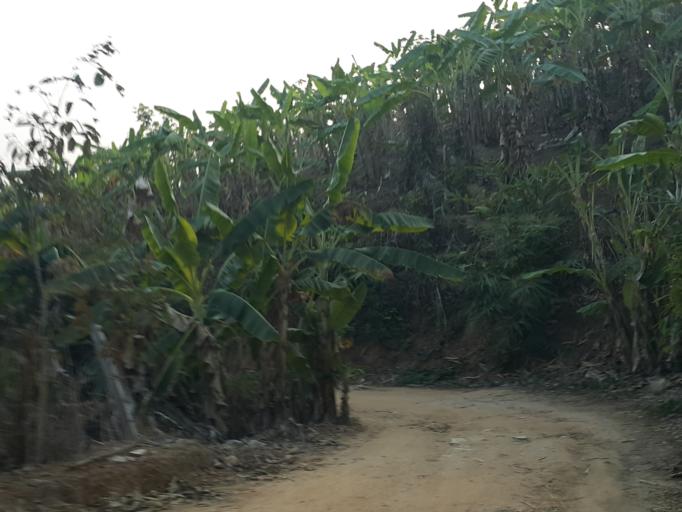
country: TH
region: Chiang Mai
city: Mae Taeng
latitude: 19.1159
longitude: 98.8275
